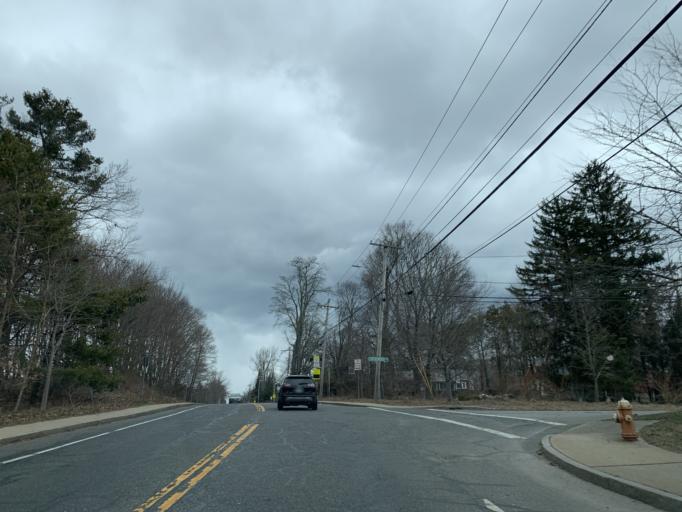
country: US
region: Massachusetts
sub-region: Norfolk County
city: Franklin
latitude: 42.0694
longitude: -71.3956
